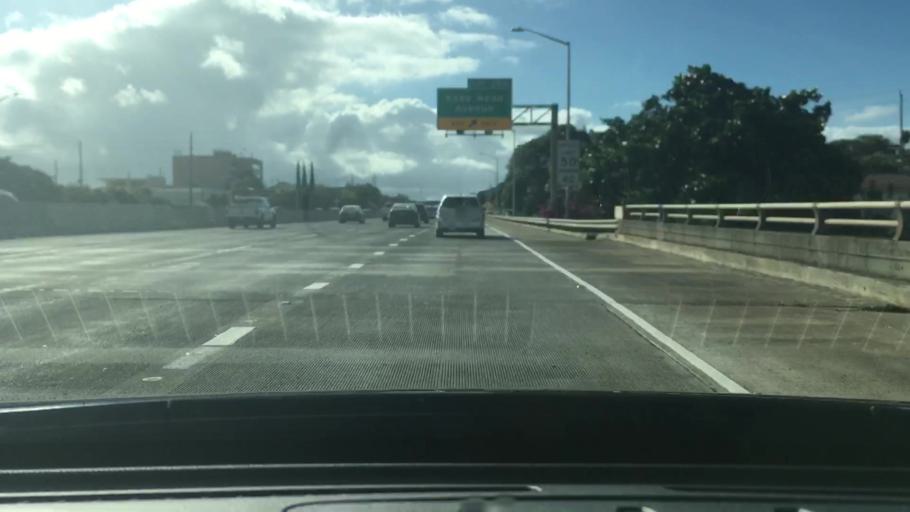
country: US
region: Hawaii
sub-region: Honolulu County
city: Honolulu
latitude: 21.2814
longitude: -157.8027
